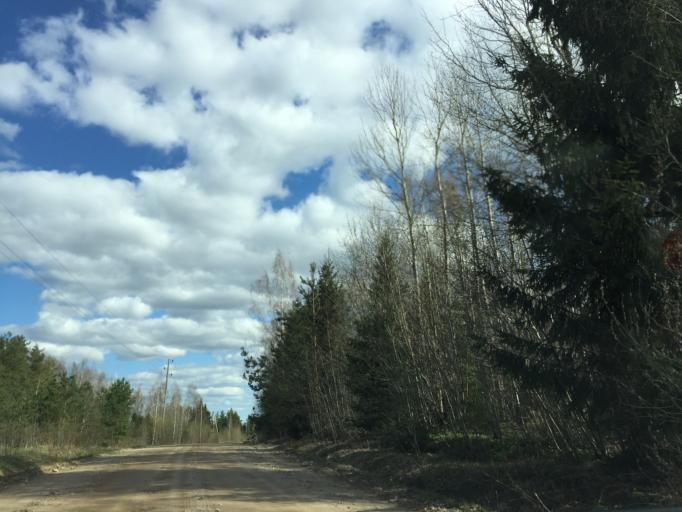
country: LV
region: Rezekne
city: Rezekne
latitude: 56.6555
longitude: 27.2791
